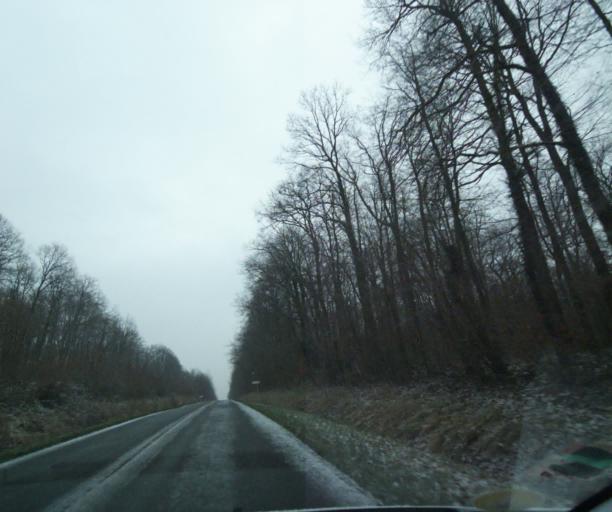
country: FR
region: Champagne-Ardenne
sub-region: Departement de la Haute-Marne
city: Wassy
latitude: 48.4745
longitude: 5.0173
